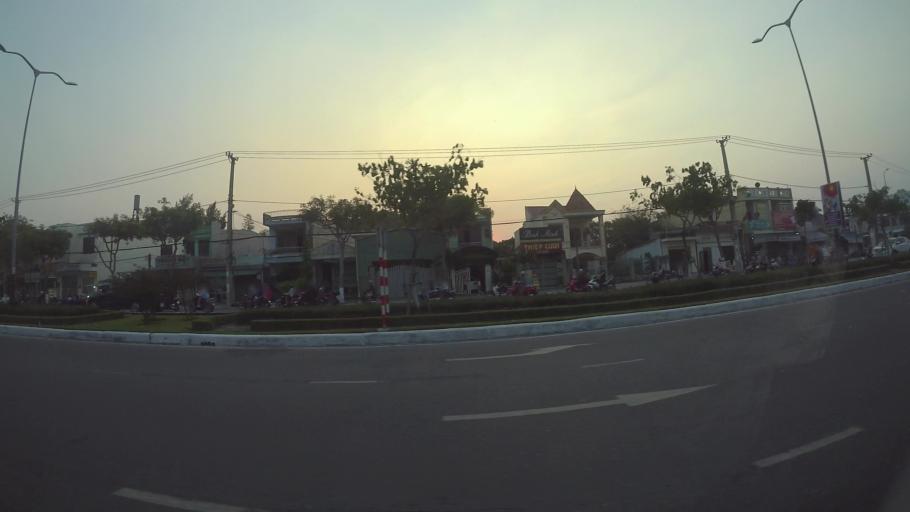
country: VN
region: Da Nang
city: Ngu Hanh Son
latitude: 16.0055
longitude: 108.2596
